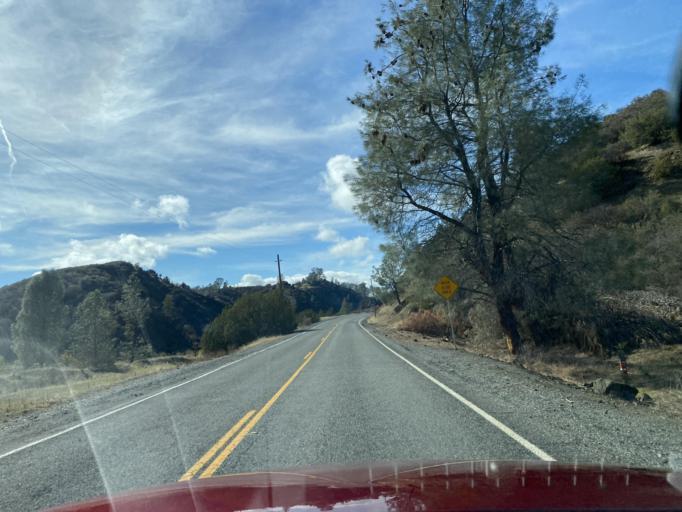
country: US
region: California
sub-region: Glenn County
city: Willows
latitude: 39.4288
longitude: -122.5113
